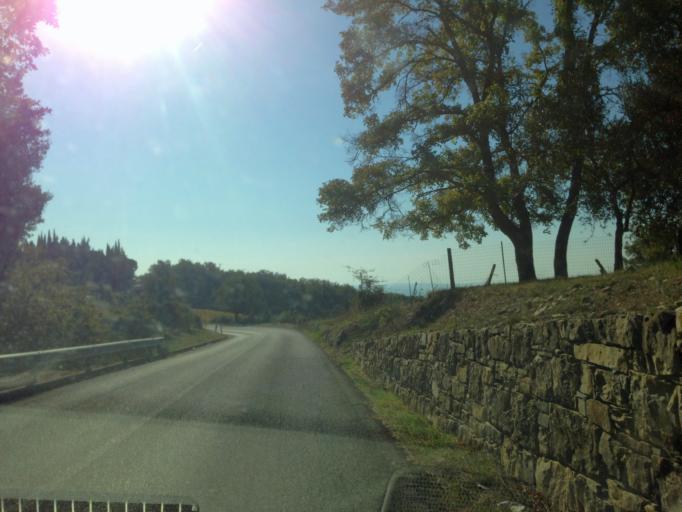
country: IT
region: Tuscany
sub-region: Provincia di Siena
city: Castellina in Chianti
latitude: 43.4509
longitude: 11.2931
